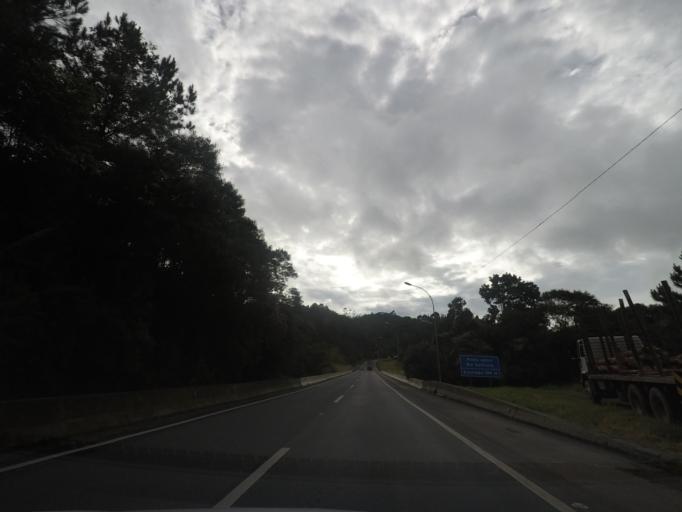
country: BR
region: Parana
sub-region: Campina Grande Do Sul
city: Campina Grande do Sul
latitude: -25.1112
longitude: -48.8459
